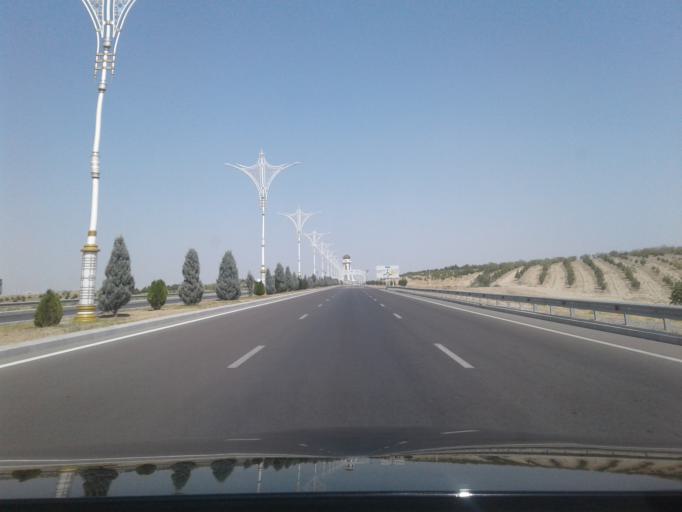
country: TM
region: Ahal
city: Ashgabat
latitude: 37.8782
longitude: 58.4139
